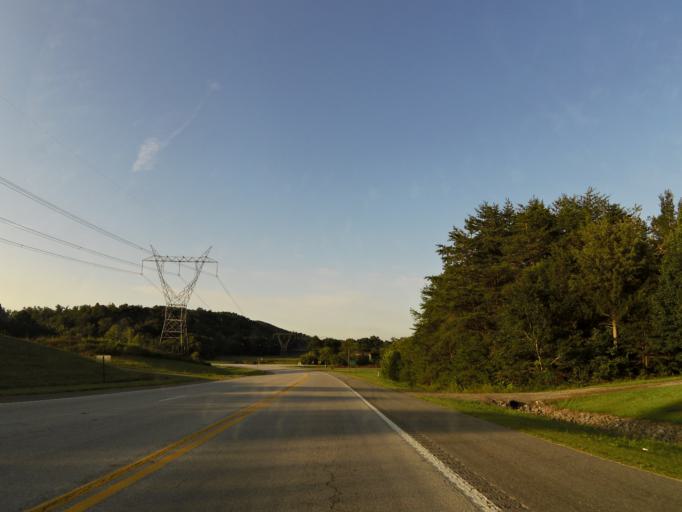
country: US
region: Tennessee
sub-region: Meigs County
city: Decatur
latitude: 35.6028
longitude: -84.6756
